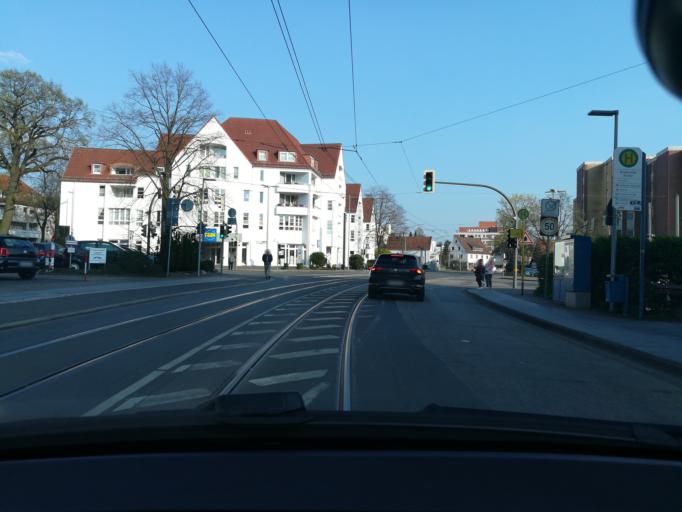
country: DE
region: North Rhine-Westphalia
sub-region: Regierungsbezirk Detmold
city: Bielefeld
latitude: 51.9880
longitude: 8.5143
